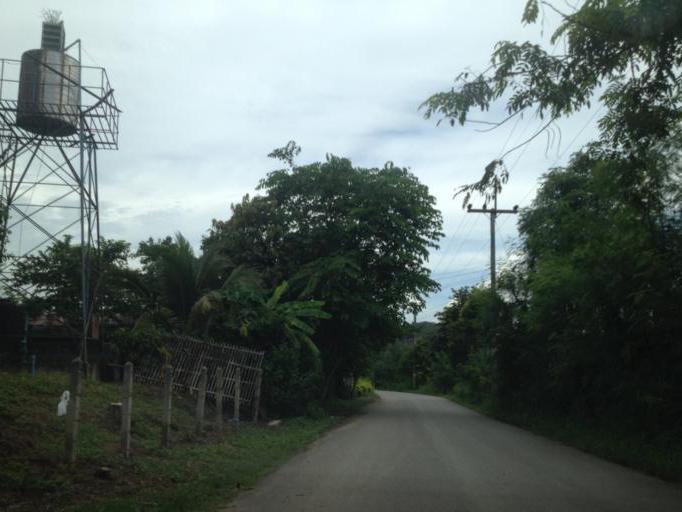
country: TH
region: Chiang Mai
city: Hang Dong
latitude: 18.6984
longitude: 98.8644
